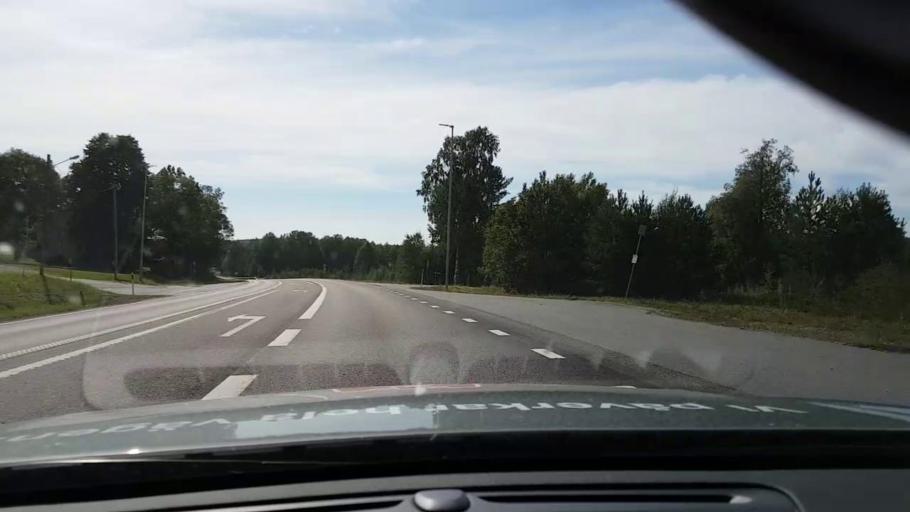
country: SE
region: Vaesternorrland
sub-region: OErnskoeldsviks Kommun
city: Husum
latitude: 63.3357
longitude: 19.0670
